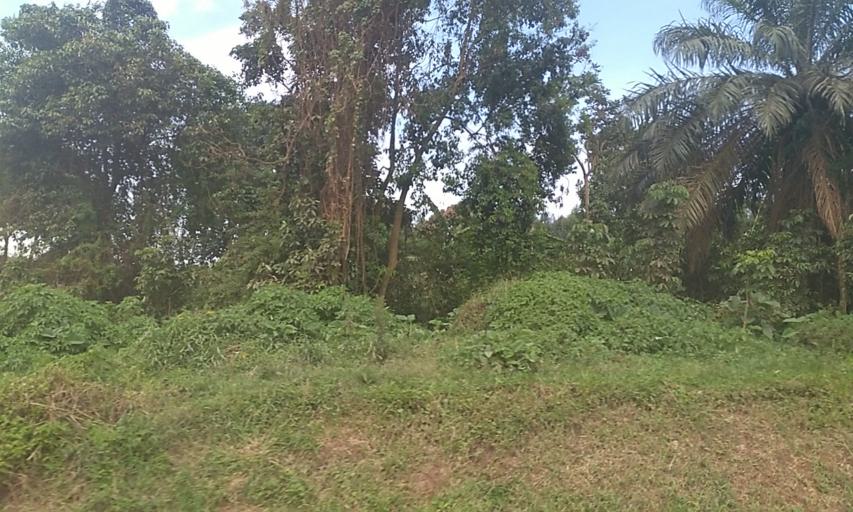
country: UG
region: Central Region
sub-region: Wakiso District
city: Kajansi
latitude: 0.2761
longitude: 32.5151
